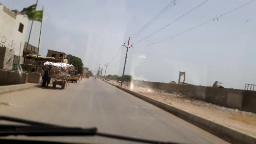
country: PK
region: Sindh
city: Malir Cantonment
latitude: 24.8368
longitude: 67.2051
